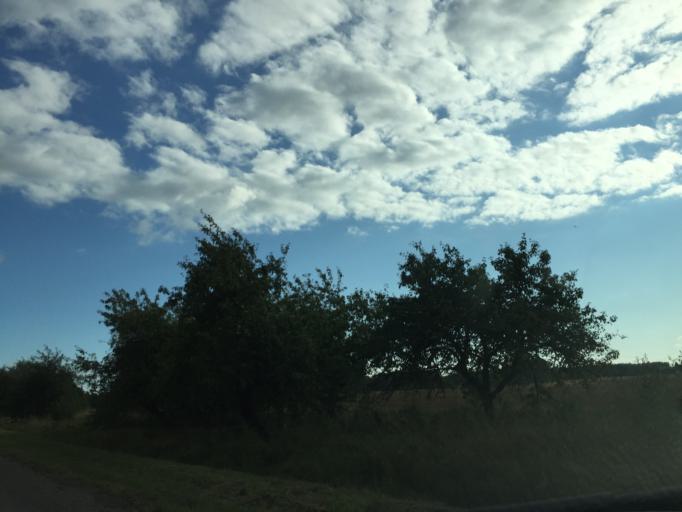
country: LV
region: Krimulda
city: Ragana
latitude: 57.2867
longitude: 24.6579
